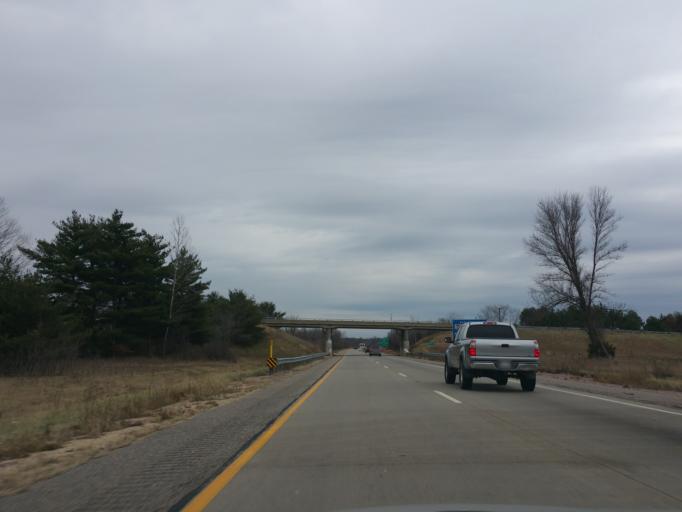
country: US
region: Wisconsin
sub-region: Juneau County
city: New Lisbon
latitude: 43.8948
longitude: -90.1742
